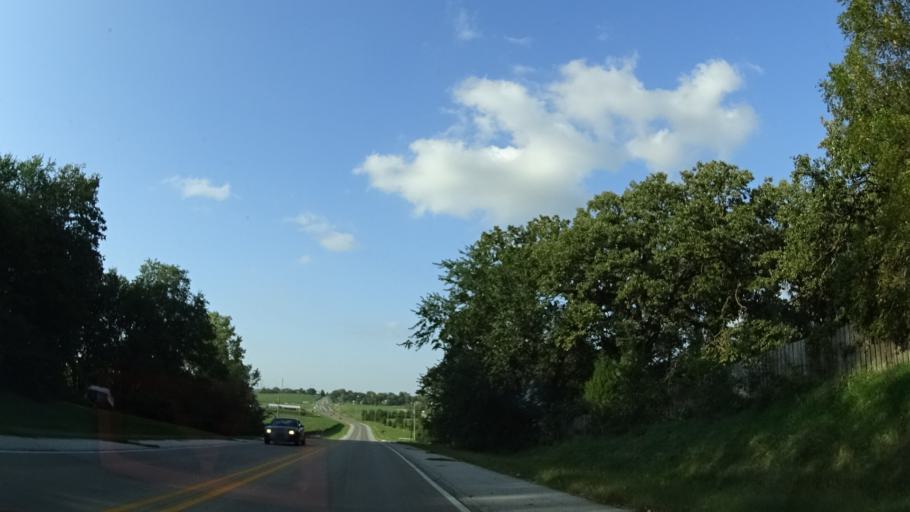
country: US
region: Nebraska
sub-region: Sarpy County
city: Offutt Air Force Base
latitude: 41.1533
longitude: -95.9666
